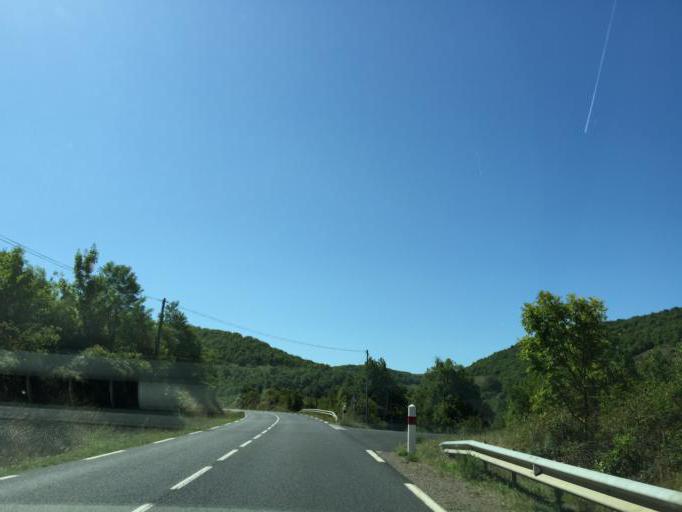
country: FR
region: Midi-Pyrenees
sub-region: Departement de l'Aveyron
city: Saint-Georges-de-Luzencon
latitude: 44.0358
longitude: 2.9178
